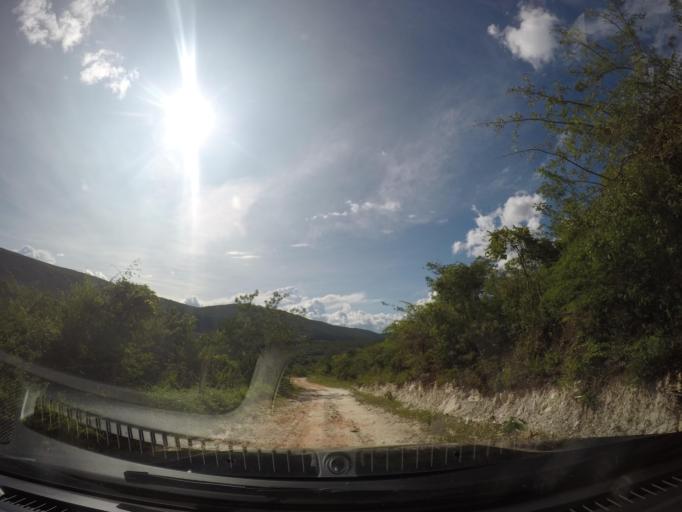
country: BR
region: Bahia
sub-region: Livramento Do Brumado
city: Livramento do Brumado
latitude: -13.2158
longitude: -41.6029
